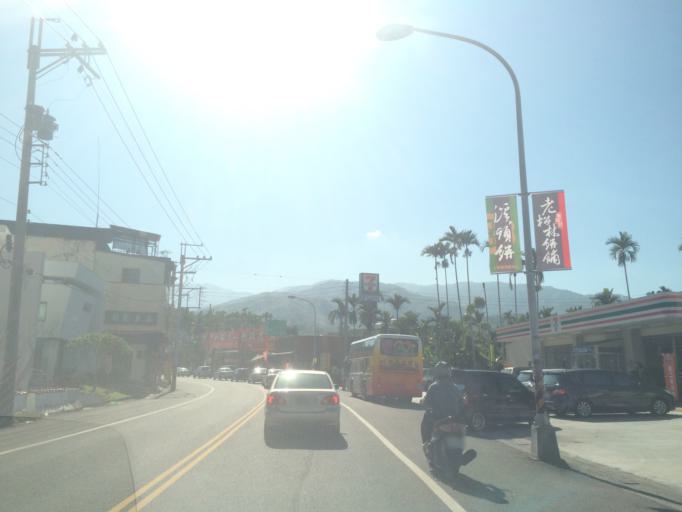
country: TW
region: Taiwan
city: Lugu
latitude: 23.7373
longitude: 120.7600
